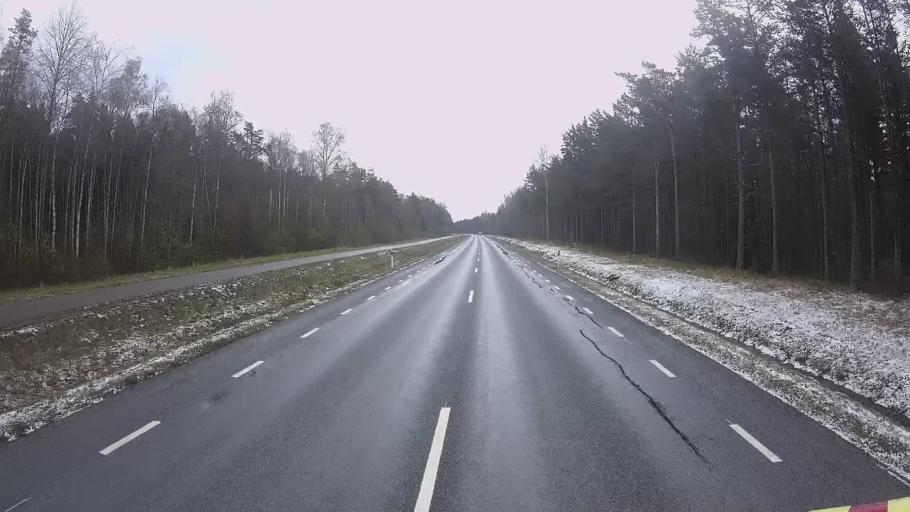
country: EE
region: Hiiumaa
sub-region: Kaerdla linn
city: Kardla
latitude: 59.0004
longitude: 22.7001
